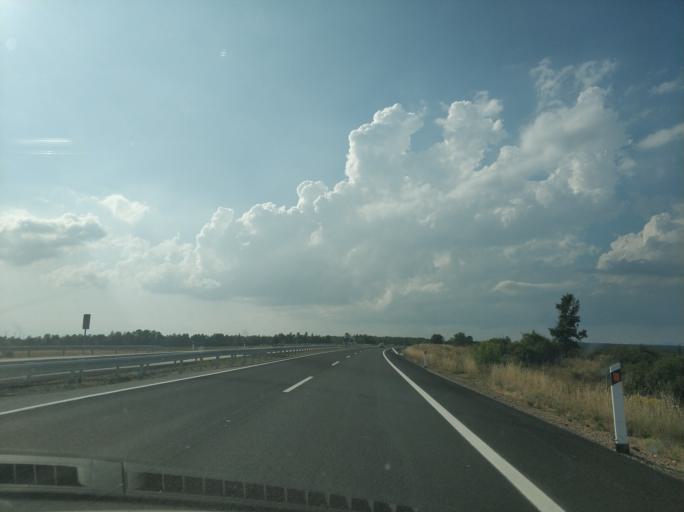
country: ES
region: Castille and Leon
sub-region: Provincia de Leon
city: Cimanes del Tejar
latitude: 42.6169
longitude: -5.7361
